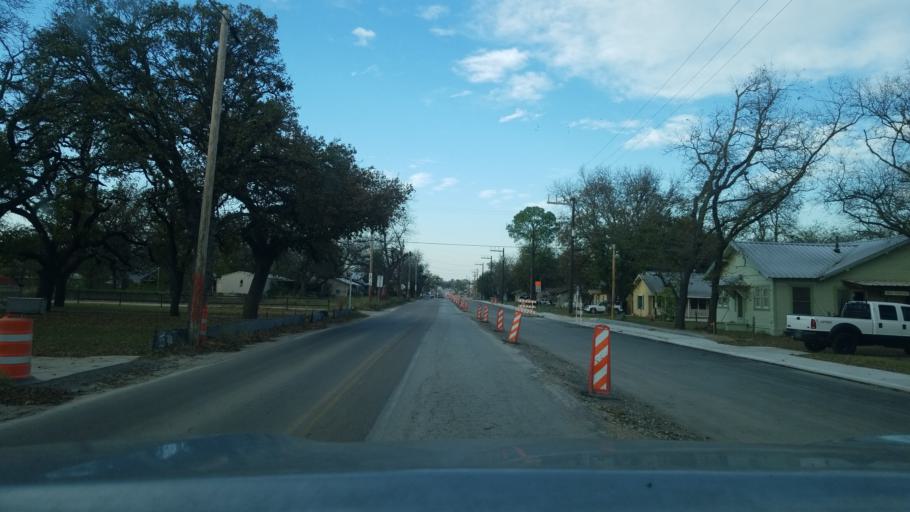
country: US
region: Texas
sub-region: Brown County
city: Lake Brownwood
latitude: 32.0916
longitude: -98.9640
